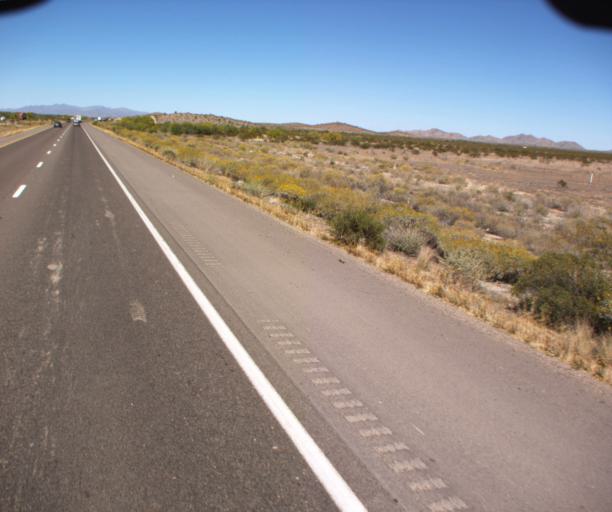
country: US
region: Arizona
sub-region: Maricopa County
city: Buckeye
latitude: 33.2374
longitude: -112.6402
